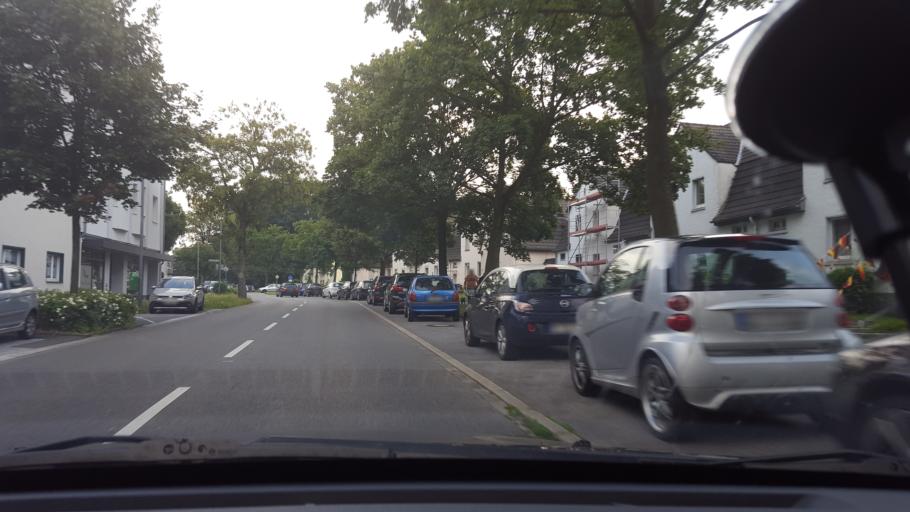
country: DE
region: North Rhine-Westphalia
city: Herten
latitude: 51.6136
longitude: 7.1258
